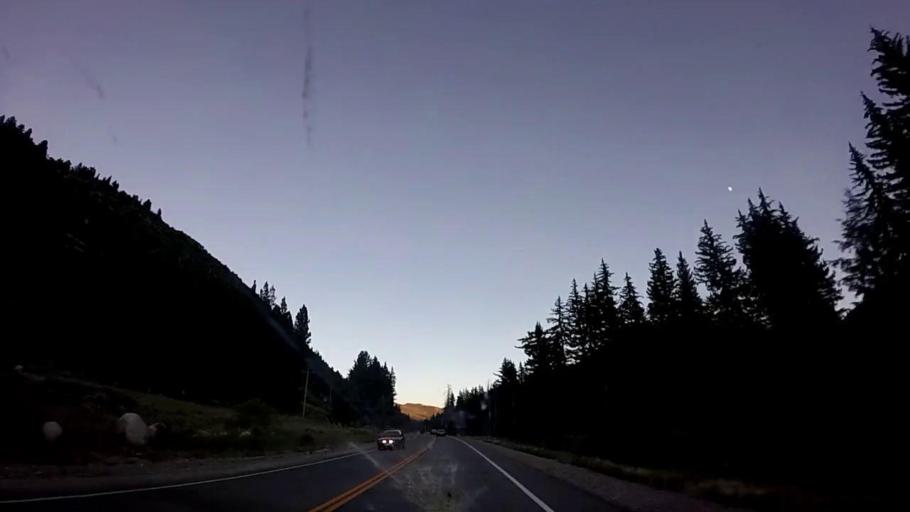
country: US
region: Utah
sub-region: Summit County
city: Summit Park
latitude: 40.6441
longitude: -111.6398
